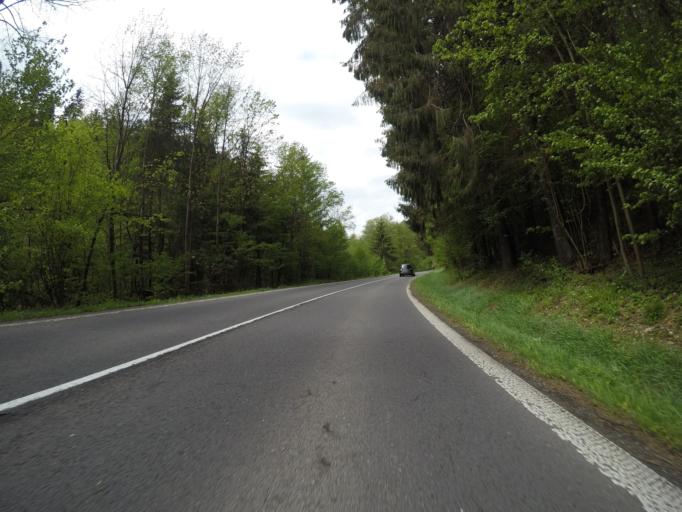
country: SK
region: Banskobystricky
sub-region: Okres Banska Bystrica
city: Brezno
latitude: 48.8372
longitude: 19.5858
